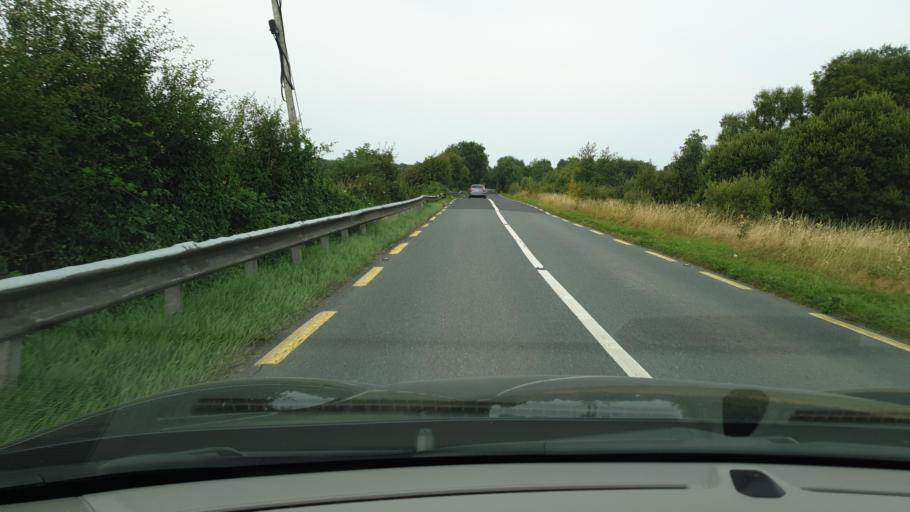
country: IE
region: Leinster
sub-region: An Mhi
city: Trim
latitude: 53.6342
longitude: -6.8152
